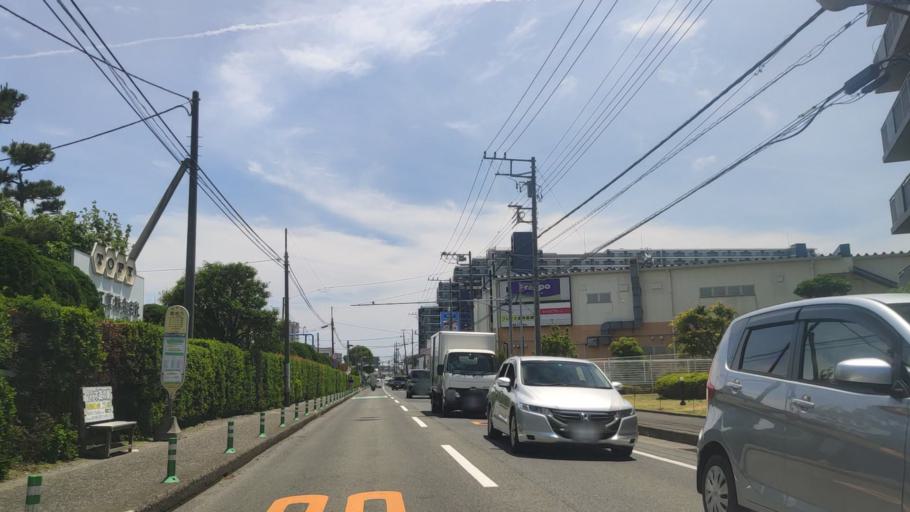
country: JP
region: Kanagawa
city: Chigasaki
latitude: 35.3361
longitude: 139.3987
